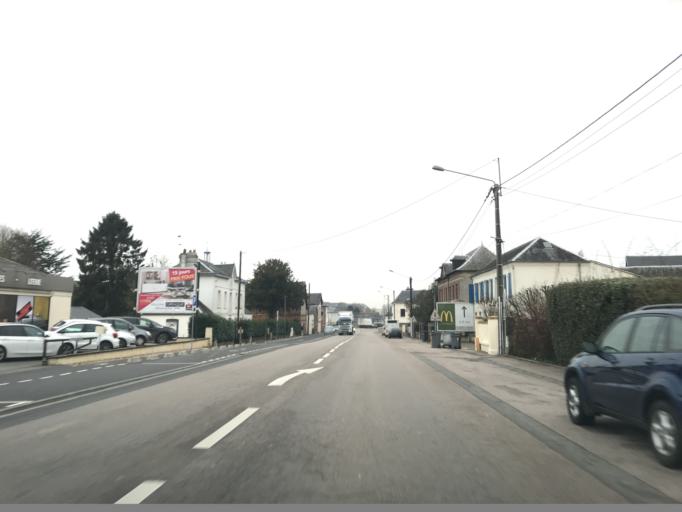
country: FR
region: Haute-Normandie
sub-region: Departement de la Seine-Maritime
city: Boos
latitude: 49.3885
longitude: 1.2047
